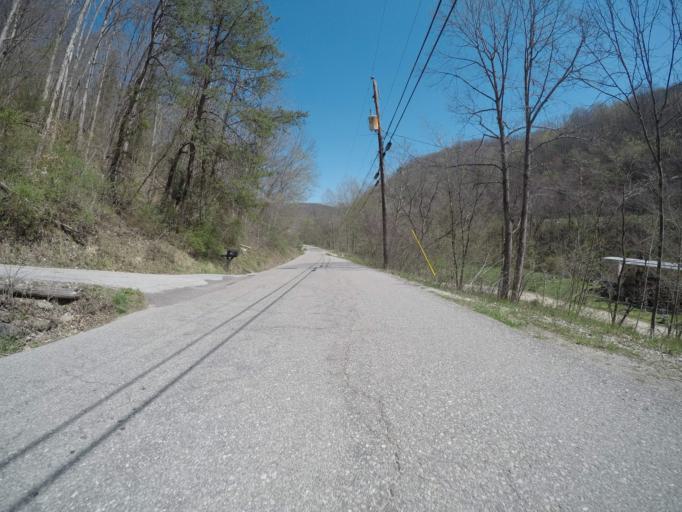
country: US
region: West Virginia
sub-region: Kanawha County
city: Pinch
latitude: 38.4136
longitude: -81.5558
